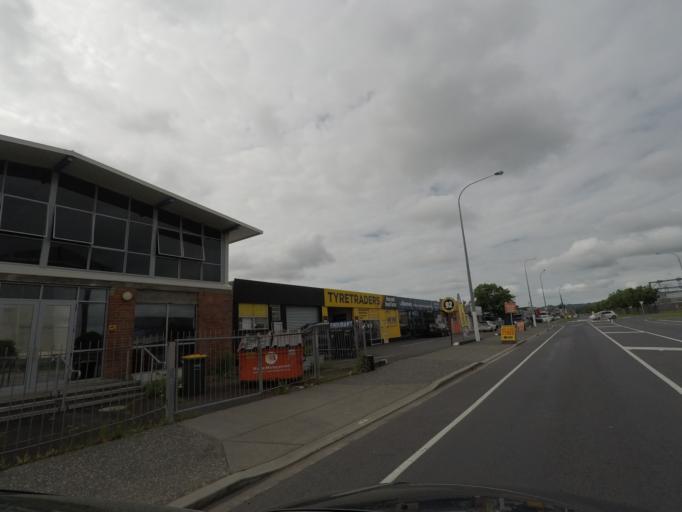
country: NZ
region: Auckland
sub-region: Auckland
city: Rosebank
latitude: -36.8847
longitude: 174.6315
